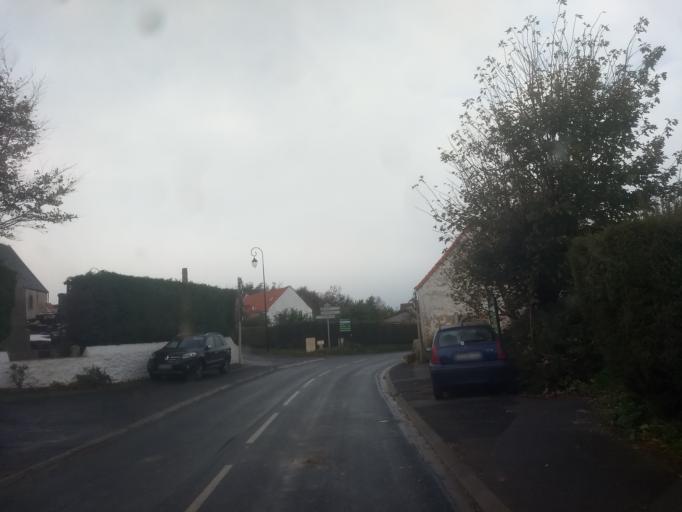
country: FR
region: Nord-Pas-de-Calais
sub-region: Departement du Pas-de-Calais
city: Wissant
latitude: 50.8823
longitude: 1.7116
